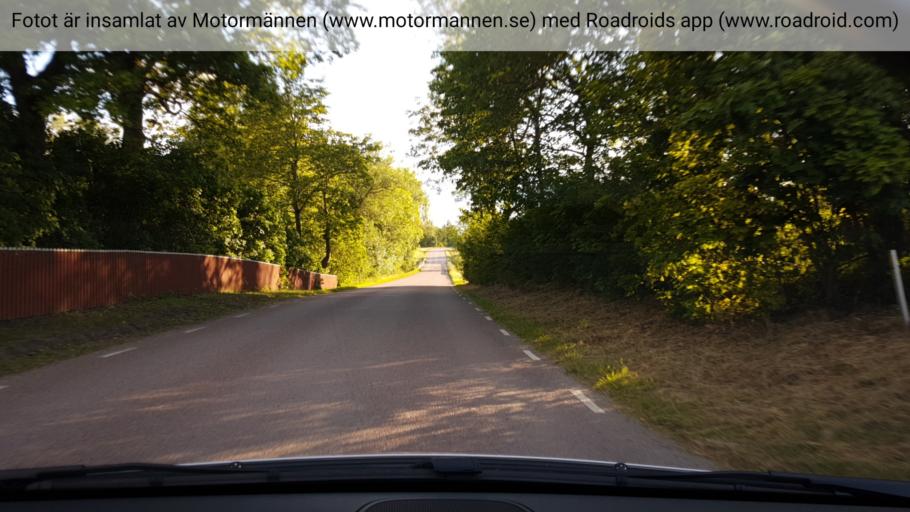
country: SE
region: Vaestmanland
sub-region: Vasteras
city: Tillberga
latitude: 59.7354
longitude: 16.7037
